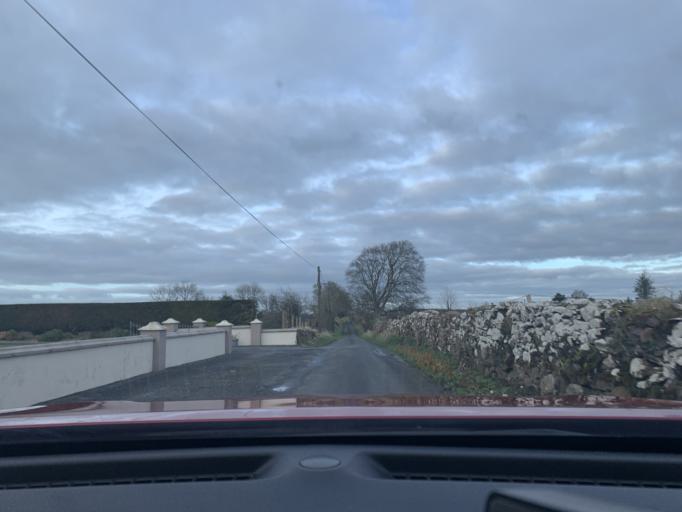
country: IE
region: Connaught
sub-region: Sligo
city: Ballymote
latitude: 54.0178
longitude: -8.5666
